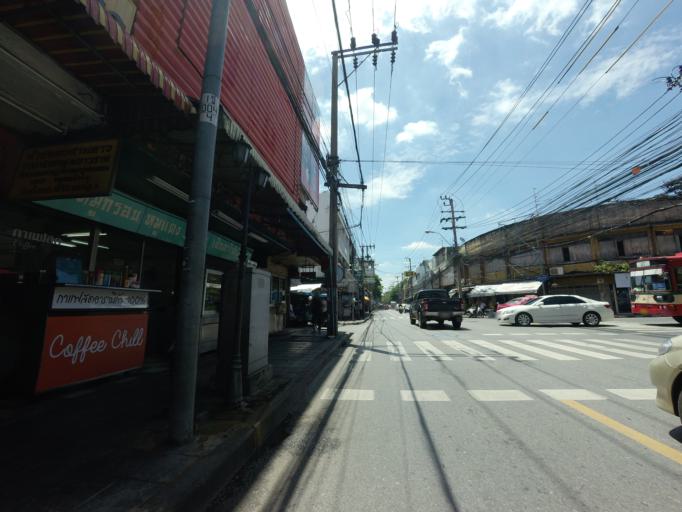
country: TH
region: Bangkok
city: Huai Khwang
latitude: 13.7896
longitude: 100.5668
